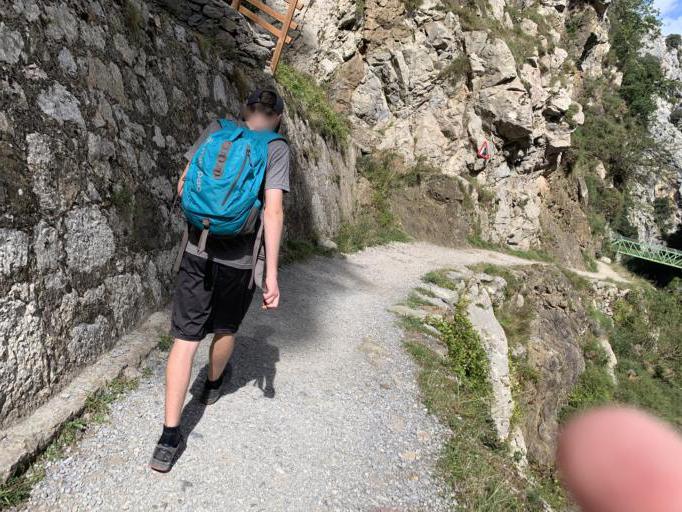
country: ES
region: Castille and Leon
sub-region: Provincia de Leon
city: Posada de Valdeon
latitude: 43.2228
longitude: -4.8956
